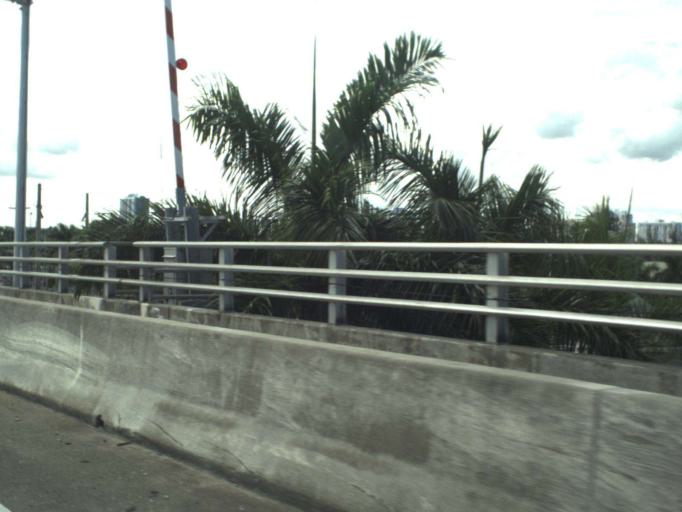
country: US
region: Florida
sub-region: Miami-Dade County
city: Sunny Isles Beach
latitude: 25.9303
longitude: -80.1309
